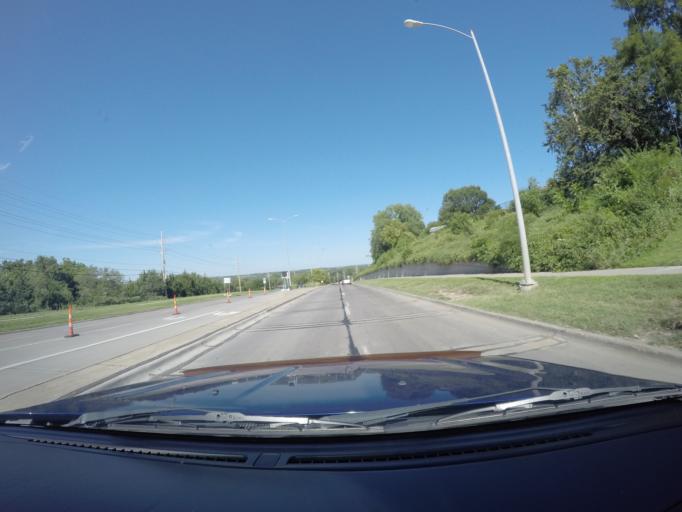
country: US
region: Kansas
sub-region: Riley County
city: Manhattan
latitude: 39.2066
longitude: -96.5753
